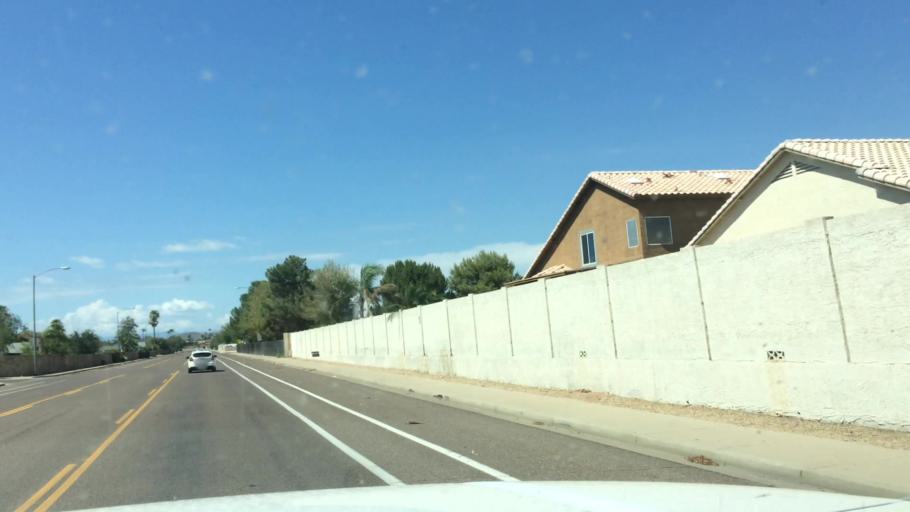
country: US
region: Arizona
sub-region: Maricopa County
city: Sun City
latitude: 33.6462
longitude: -112.2463
